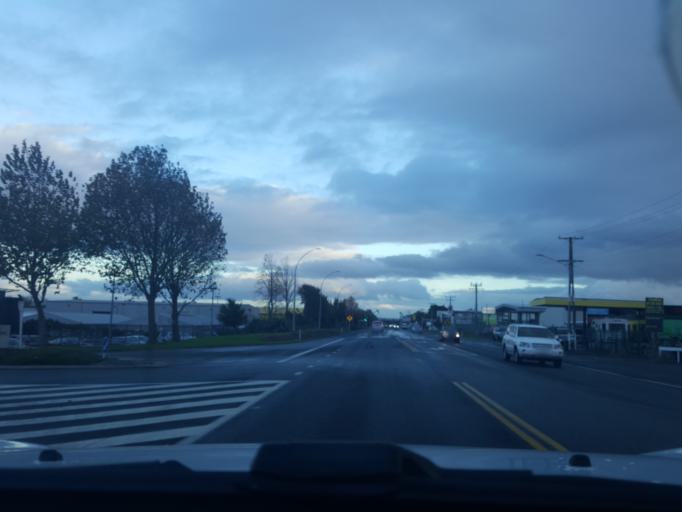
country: NZ
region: Waikato
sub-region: Hamilton City
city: Hamilton
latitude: -37.7270
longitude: 175.2187
